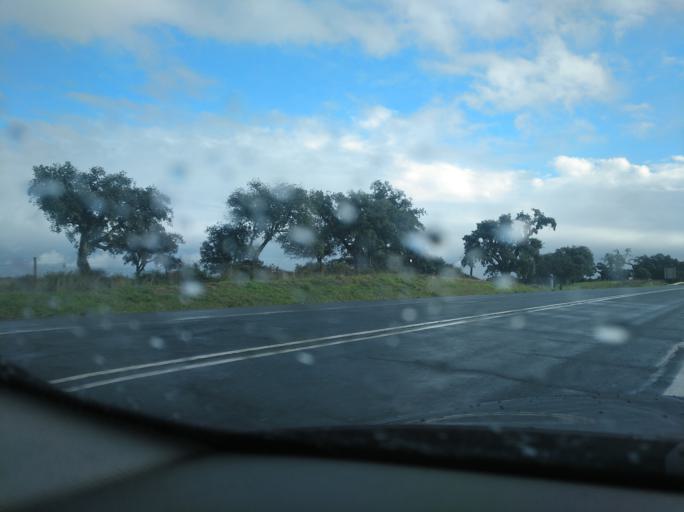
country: PT
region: Setubal
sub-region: Grandola
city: Grandola
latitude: 38.0567
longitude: -8.4043
